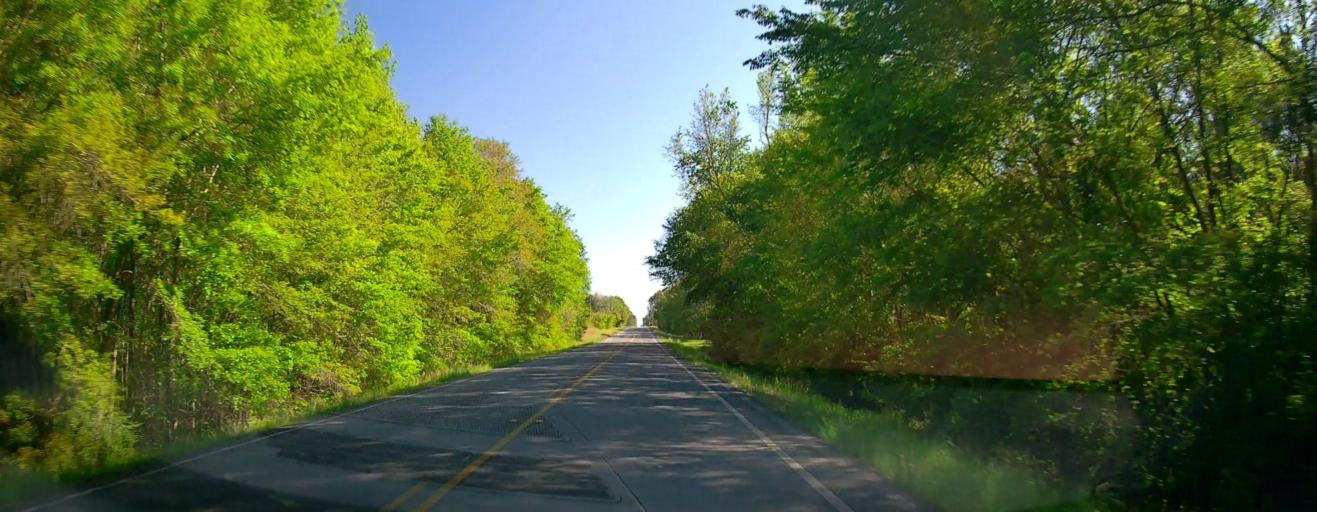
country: US
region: Georgia
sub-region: Wilcox County
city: Rochelle
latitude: 32.0940
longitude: -83.5032
